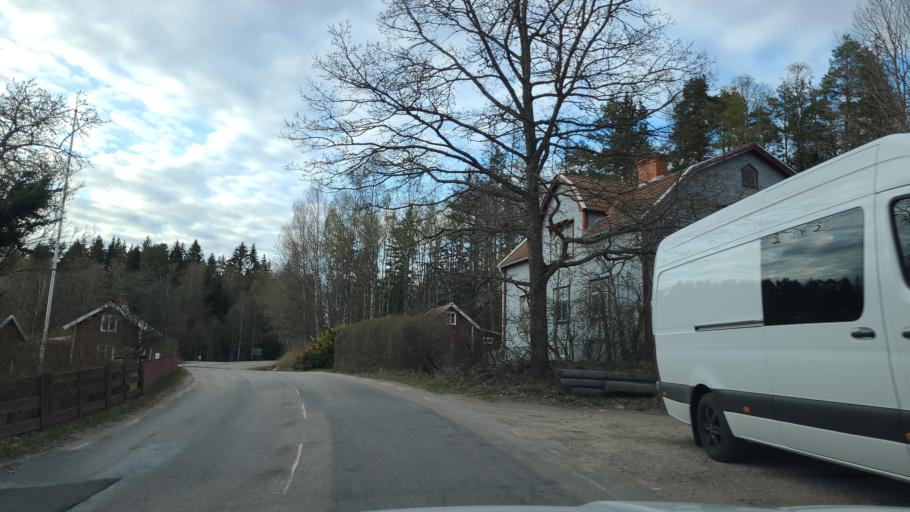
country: SE
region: Soedermanland
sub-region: Nykopings Kommun
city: Olstorp
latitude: 58.6932
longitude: 16.6369
